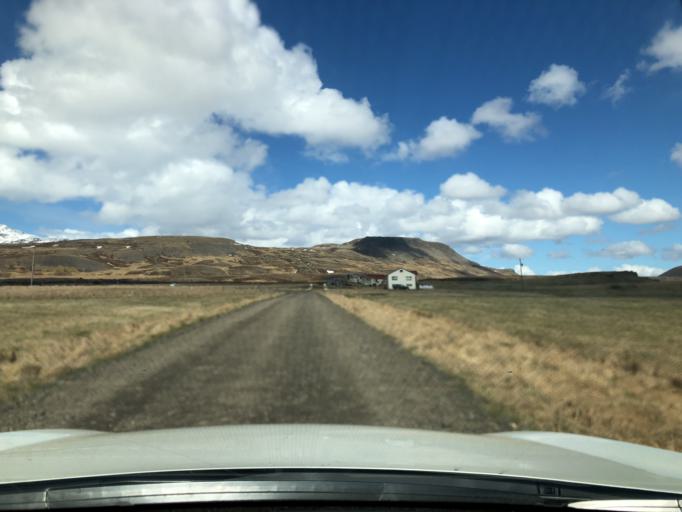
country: IS
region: West
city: Stykkisholmur
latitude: 64.8519
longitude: -22.3717
